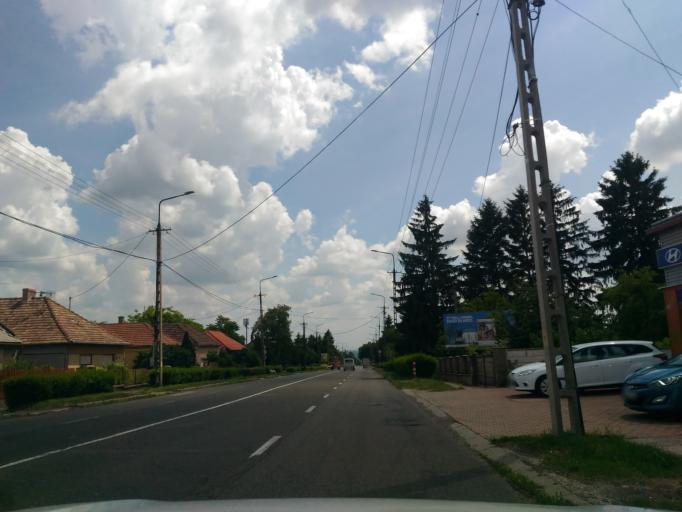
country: HU
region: Baranya
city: Pecs
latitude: 46.1096
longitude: 18.2627
